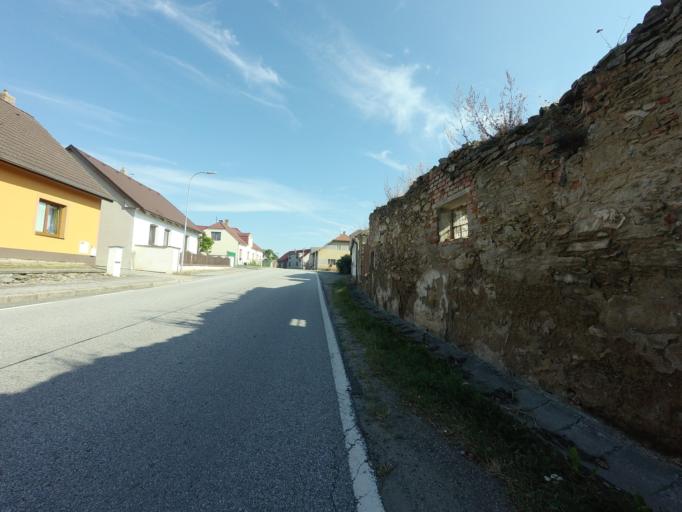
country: CZ
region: Jihocesky
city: Bernartice
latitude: 49.2968
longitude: 14.3876
